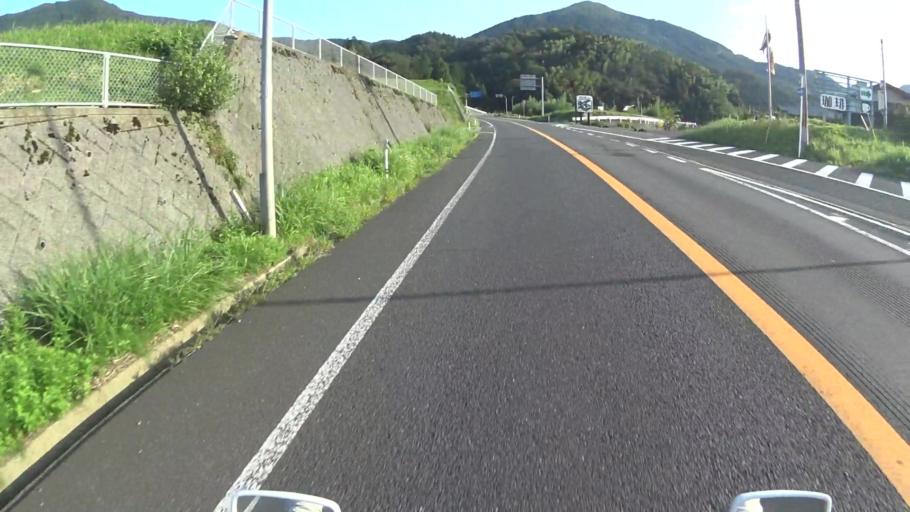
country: JP
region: Kyoto
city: Miyazu
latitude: 35.4673
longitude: 135.0848
